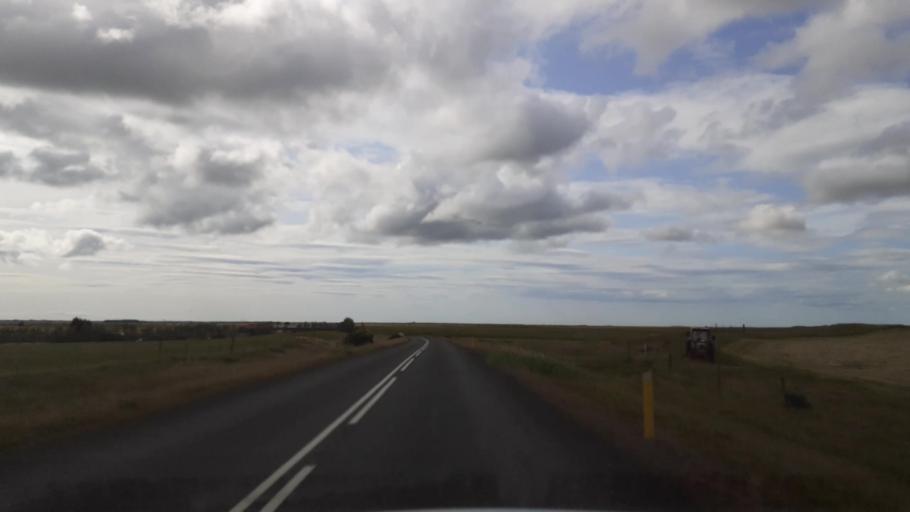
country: IS
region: South
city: Vestmannaeyjar
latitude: 63.8350
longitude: -20.4178
